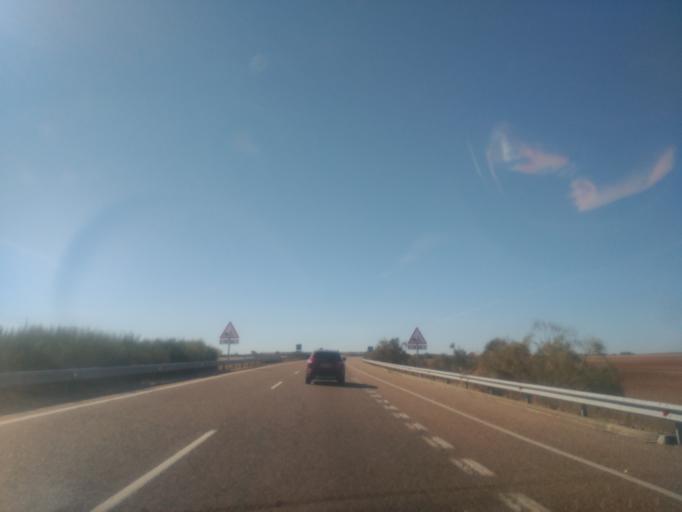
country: ES
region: Castille and Leon
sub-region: Provincia de Zamora
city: Canizal
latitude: 41.1705
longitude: -5.3781
